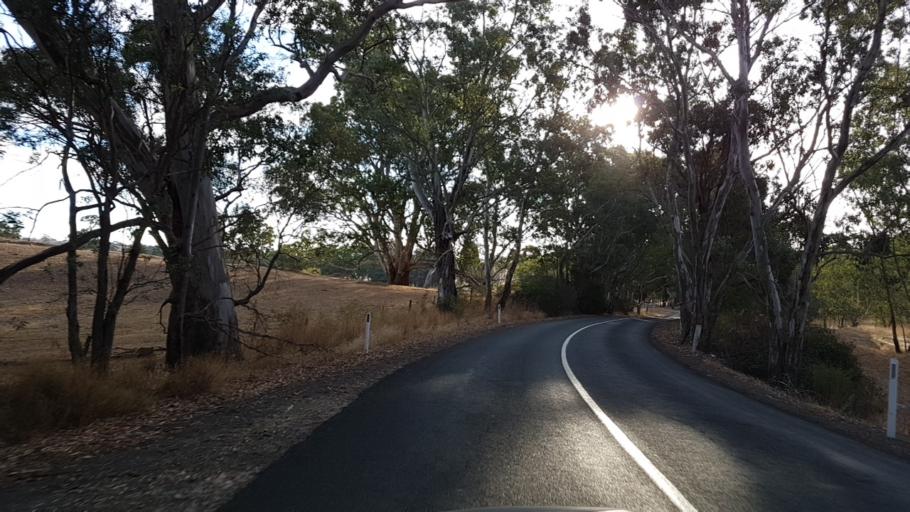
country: AU
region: South Australia
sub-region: Adelaide Hills
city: Woodside
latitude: -34.9797
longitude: 138.8909
